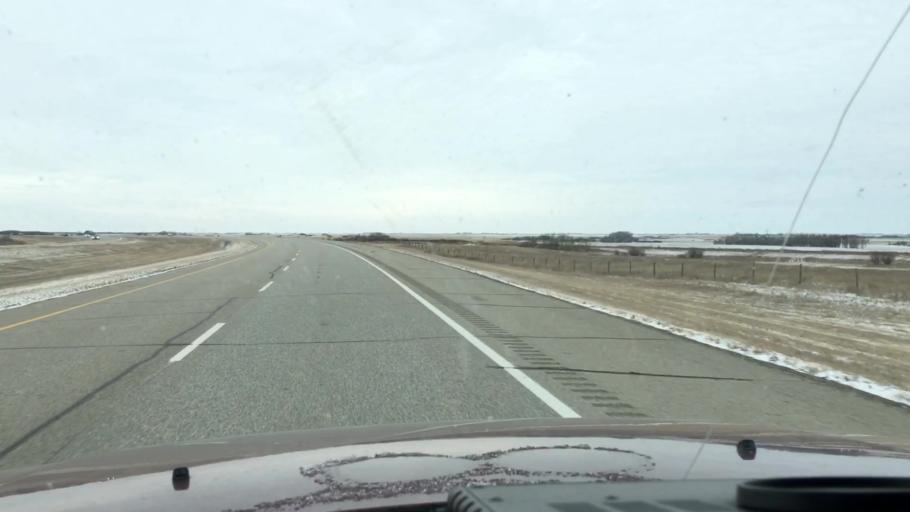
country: CA
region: Saskatchewan
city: Watrous
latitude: 51.3550
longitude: -106.1225
